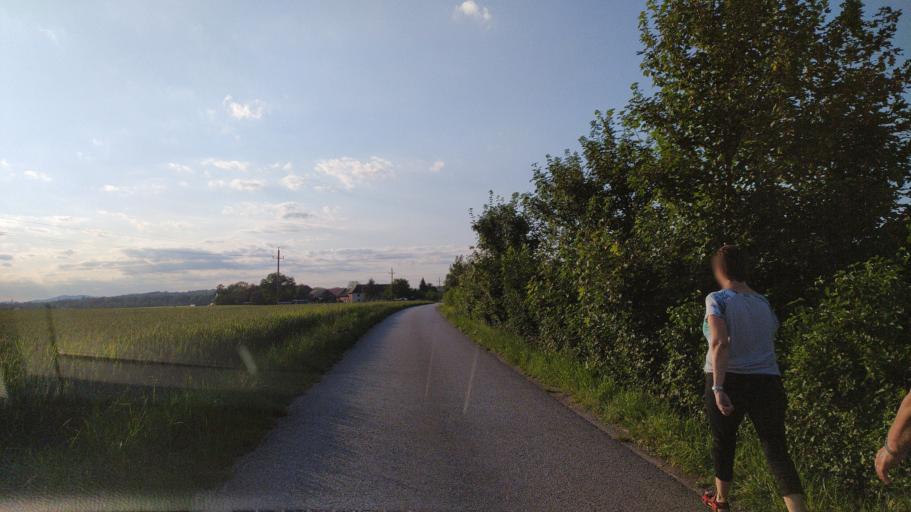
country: AT
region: Lower Austria
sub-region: Politischer Bezirk Amstetten
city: Ennsdorf
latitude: 48.2208
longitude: 14.5668
